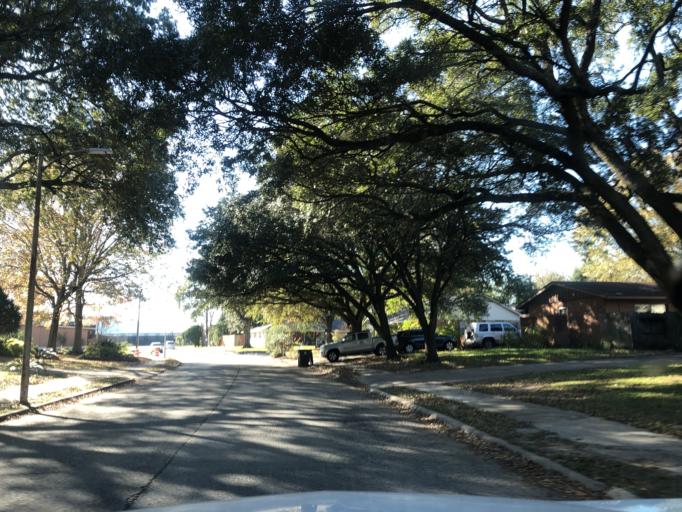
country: US
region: Texas
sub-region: Harris County
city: Bellaire
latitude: 29.6939
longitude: -95.5090
